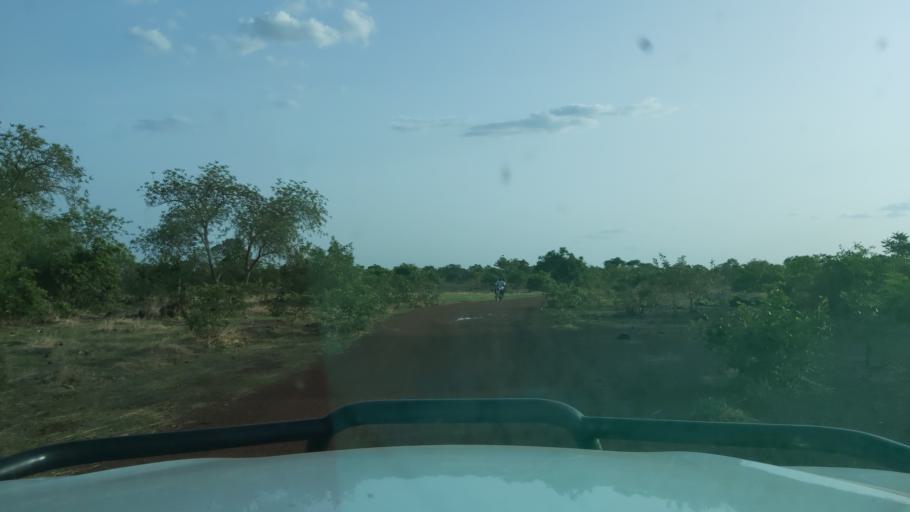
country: ML
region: Koulikoro
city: Kolokani
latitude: 13.2142
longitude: -7.8982
